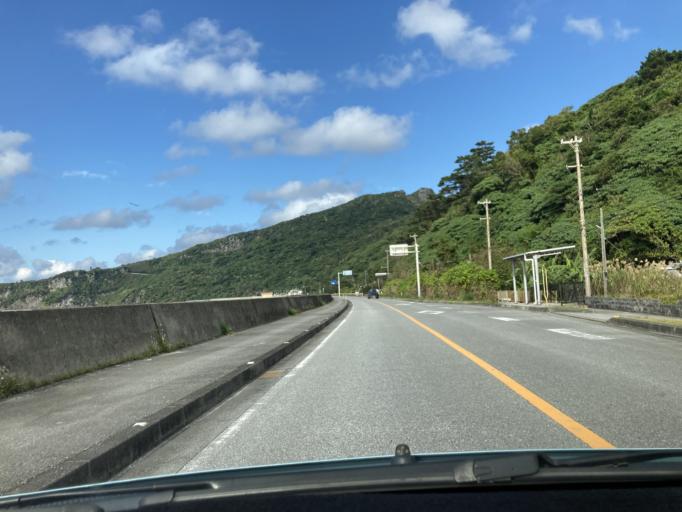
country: JP
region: Okinawa
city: Nago
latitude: 26.8424
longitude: 128.2533
